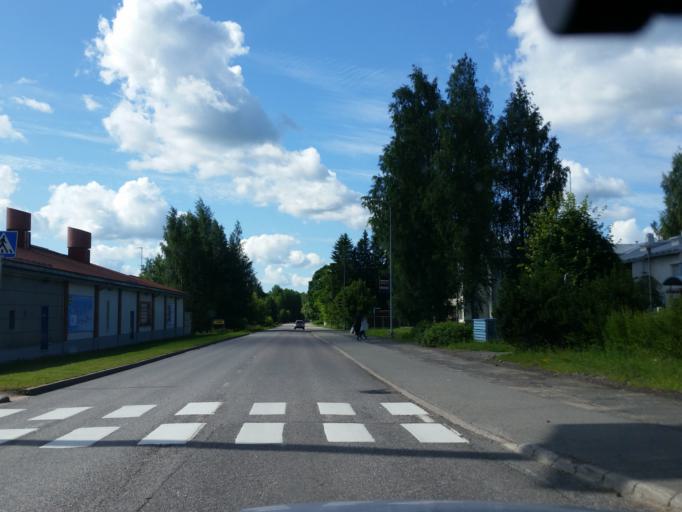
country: FI
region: Uusimaa
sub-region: Helsinki
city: Vihti
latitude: 60.3323
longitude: 24.3190
